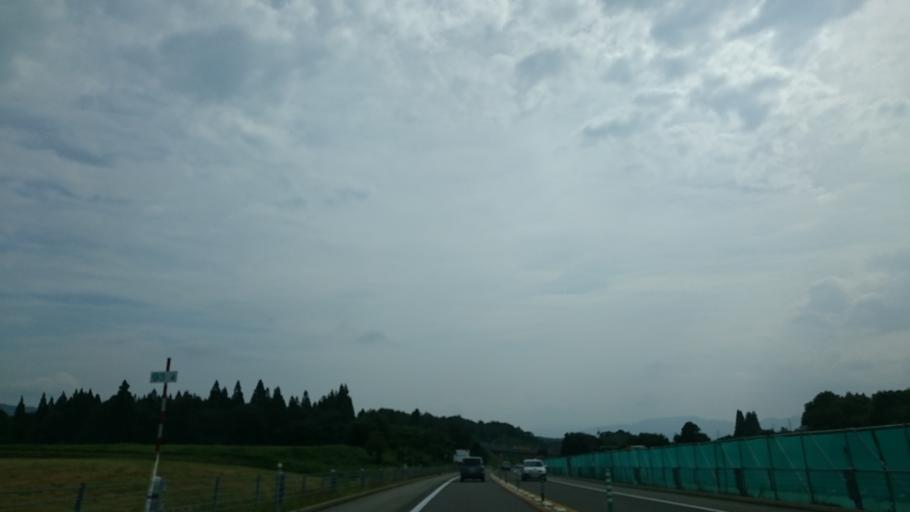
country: JP
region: Gifu
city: Gujo
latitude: 36.0002
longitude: 136.9262
